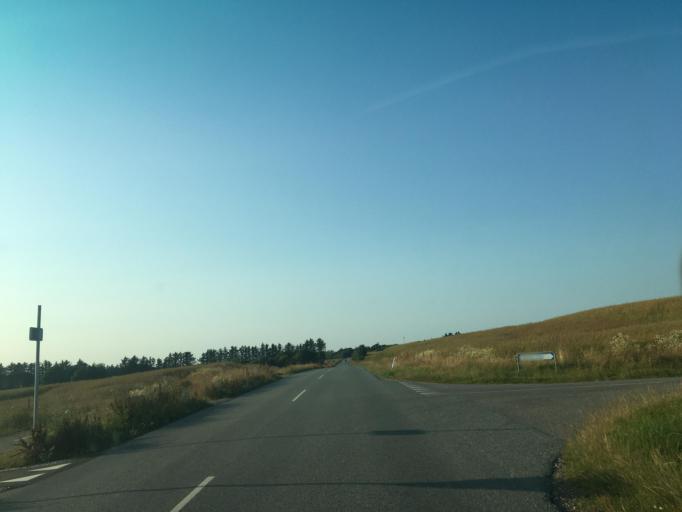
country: DK
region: North Denmark
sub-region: Thisted Kommune
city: Hurup
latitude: 56.7886
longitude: 8.4144
